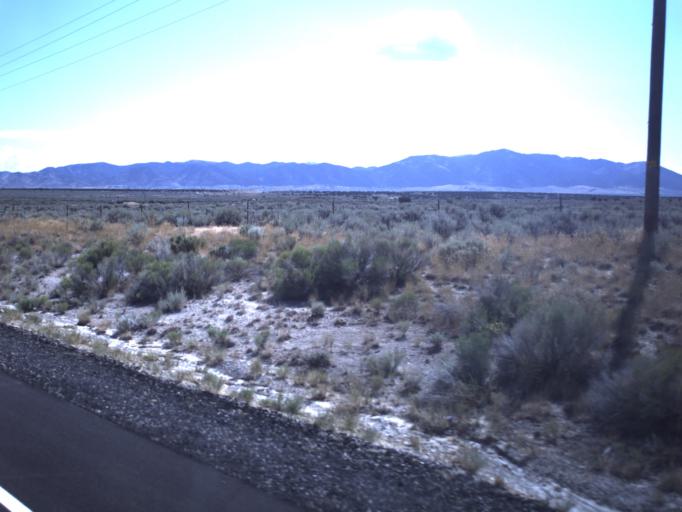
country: US
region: Utah
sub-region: Utah County
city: Eagle Mountain
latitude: 40.0741
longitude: -112.3578
